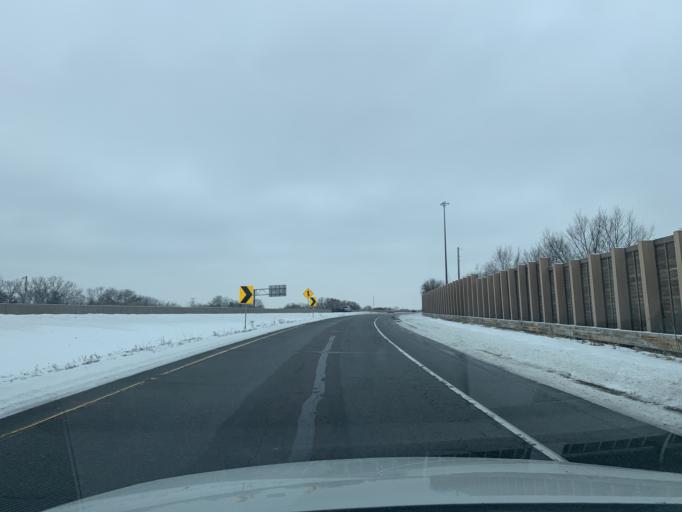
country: US
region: Minnesota
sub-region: Anoka County
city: Coon Rapids
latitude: 45.1432
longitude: -93.2729
